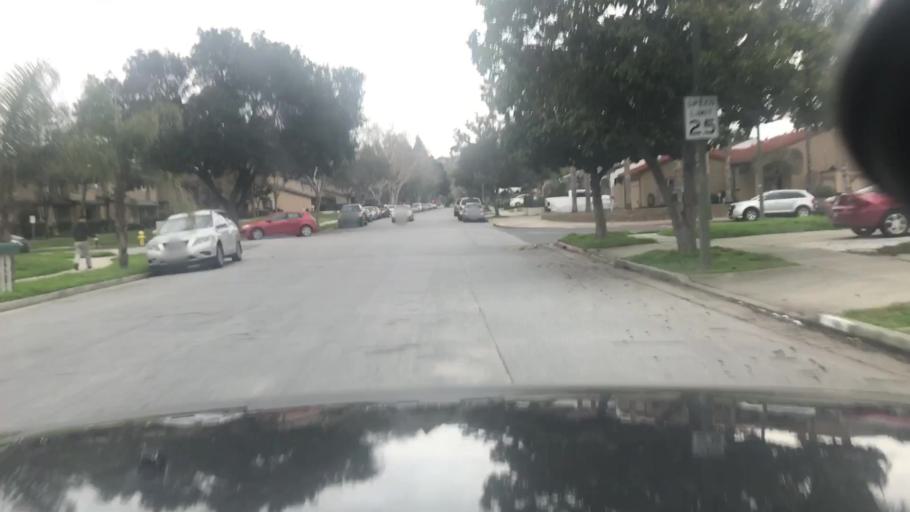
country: US
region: California
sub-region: Santa Clara County
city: Seven Trees
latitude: 37.3096
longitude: -121.8045
